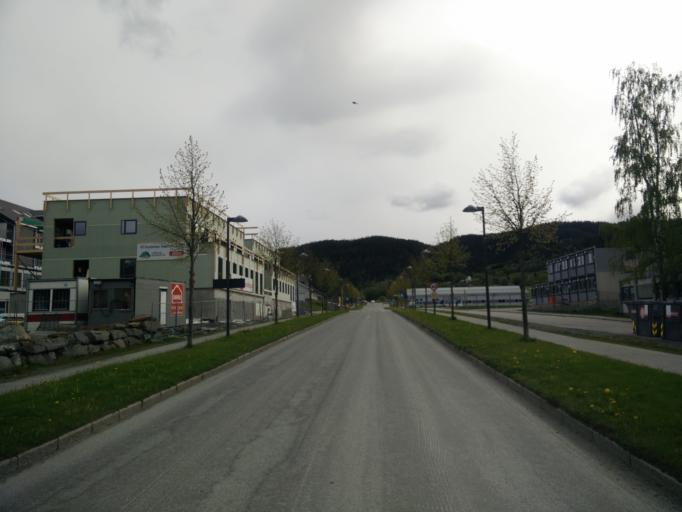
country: NO
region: Sor-Trondelag
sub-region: Skaun
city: Borsa
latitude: 63.3247
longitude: 10.0658
